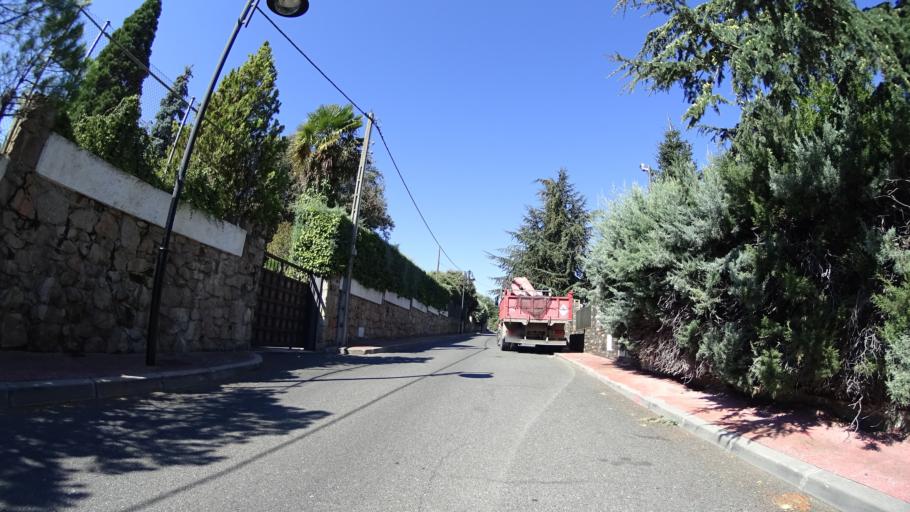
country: ES
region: Madrid
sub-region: Provincia de Madrid
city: Galapagar
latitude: 40.5931
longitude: -3.9873
